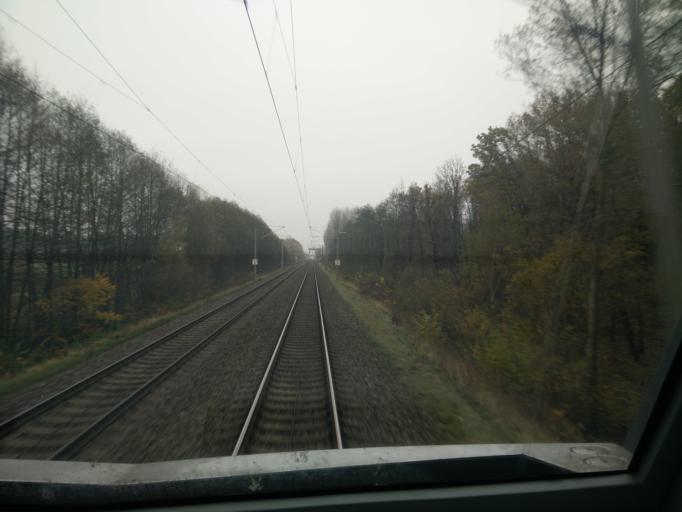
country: DE
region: Brandenburg
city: Nennhausen
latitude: 52.6013
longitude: 12.4785
